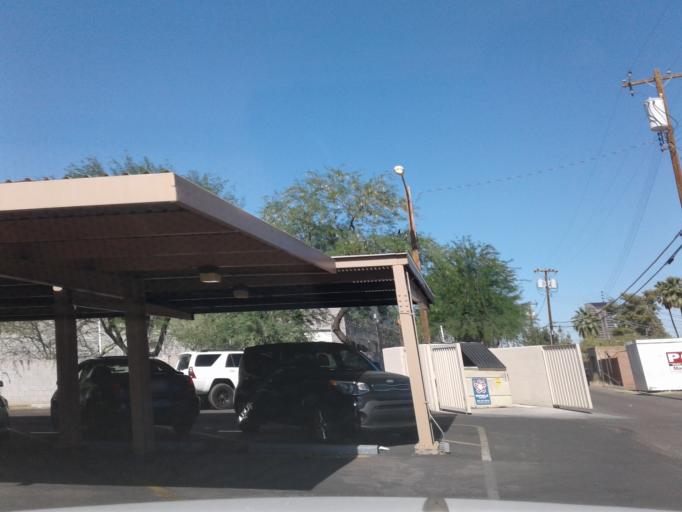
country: US
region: Arizona
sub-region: Maricopa County
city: Phoenix
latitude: 33.4666
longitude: -112.0619
